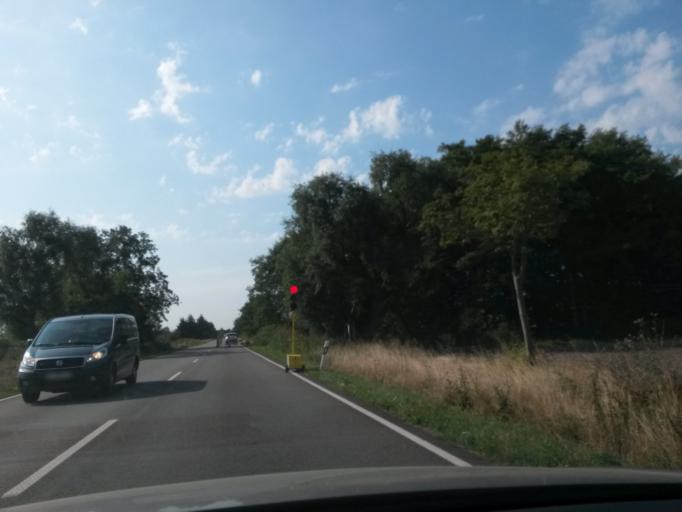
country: DE
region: Saxony-Anhalt
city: Jerichow
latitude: 52.5075
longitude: 12.0175
